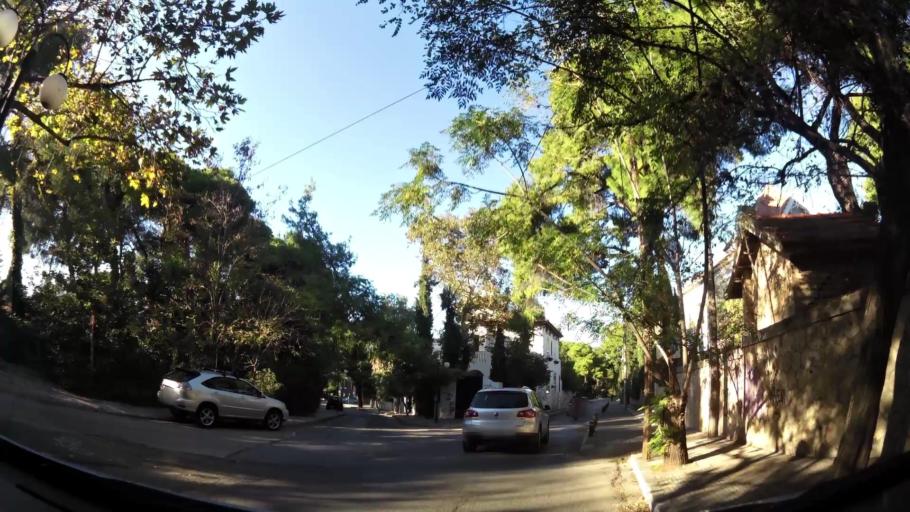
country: GR
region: Attica
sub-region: Nomarchia Athinas
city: Kifisia
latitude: 38.0824
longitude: 23.8102
